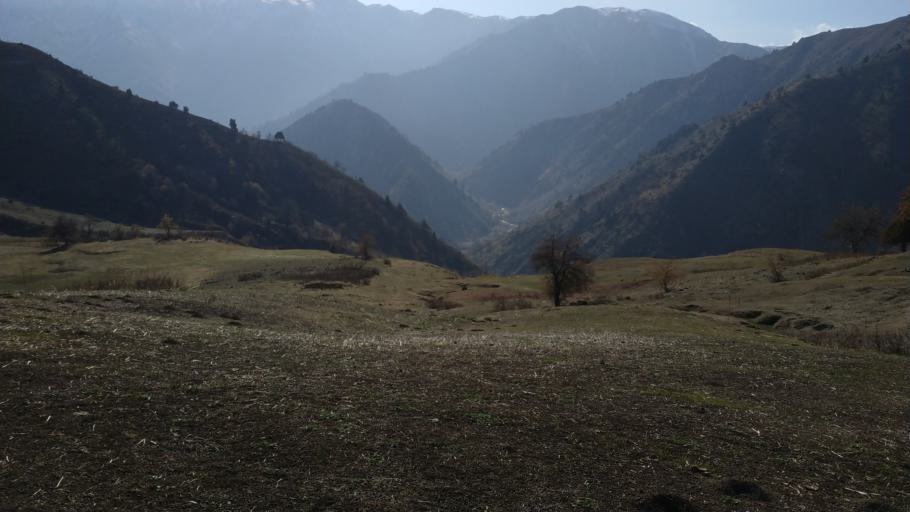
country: TJ
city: Varzob
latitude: 38.8866
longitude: 68.7791
